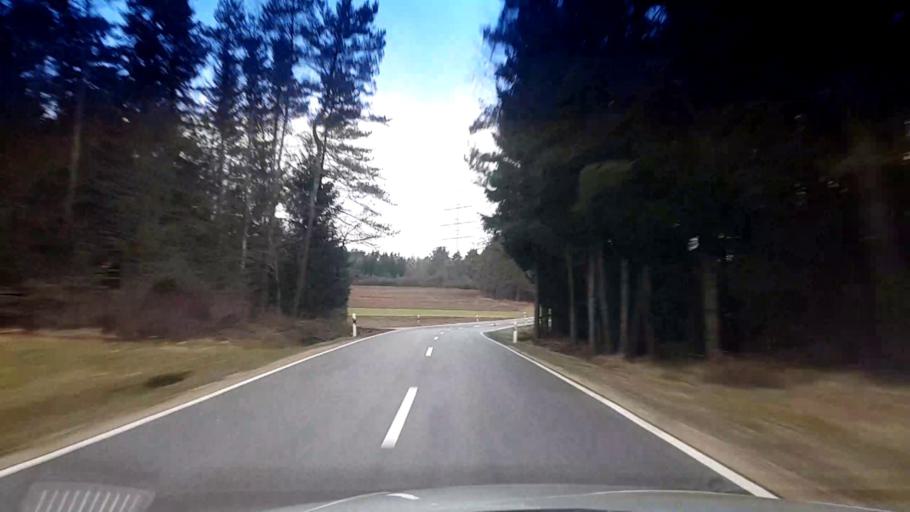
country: DE
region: Bavaria
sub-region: Upper Franconia
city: Wattendorf
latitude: 50.0163
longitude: 11.1288
